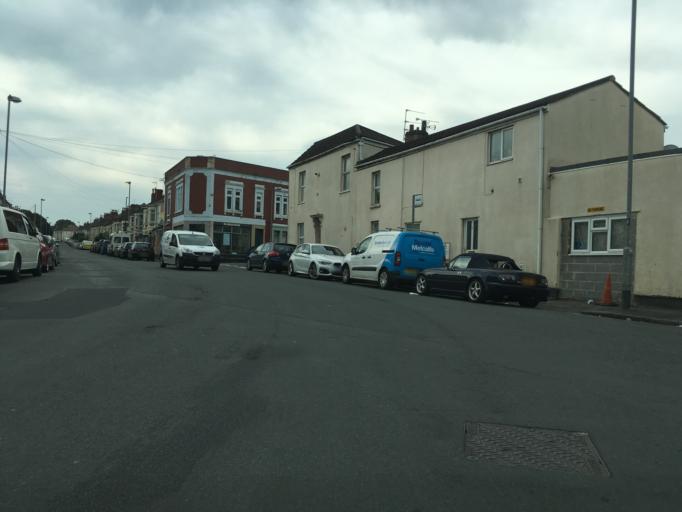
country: GB
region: England
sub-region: Bristol
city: Bristol
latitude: 51.4698
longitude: -2.5636
